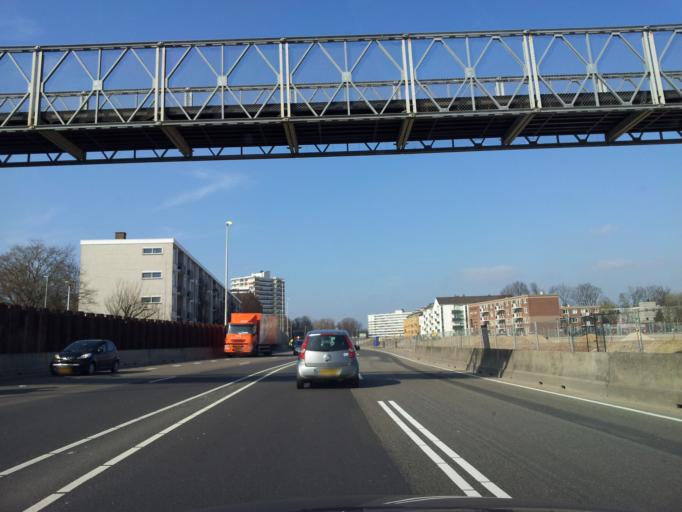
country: NL
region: Limburg
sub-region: Gemeente Maastricht
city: Heer
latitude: 50.8447
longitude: 5.7152
